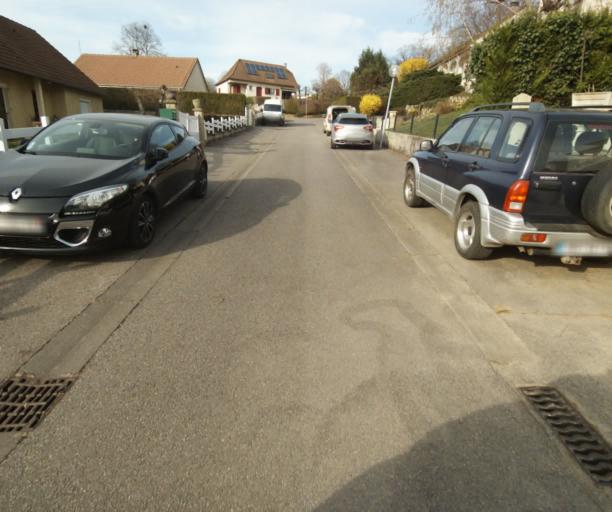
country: FR
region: Limousin
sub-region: Departement de la Correze
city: Naves
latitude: 45.3189
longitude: 1.7591
